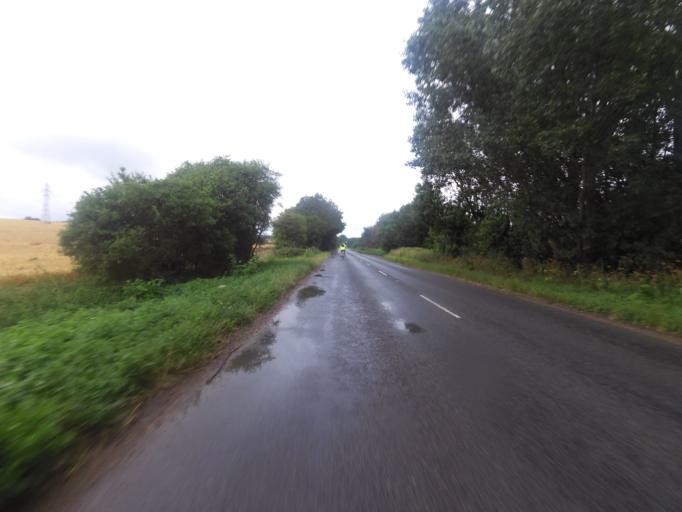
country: GB
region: England
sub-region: Suffolk
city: Bramford
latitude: 52.0867
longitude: 1.0914
